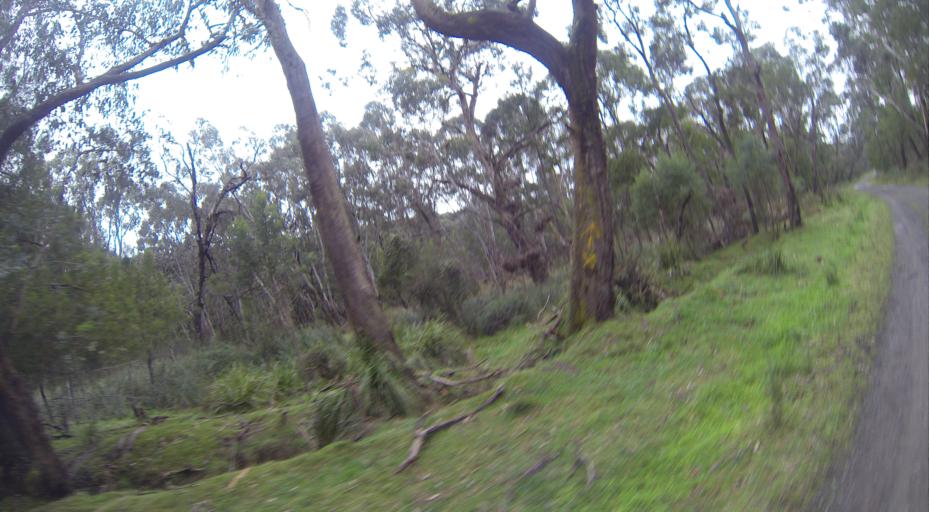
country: AU
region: Victoria
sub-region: Yarra Ranges
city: Lysterfield
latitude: -37.9539
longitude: 145.3078
